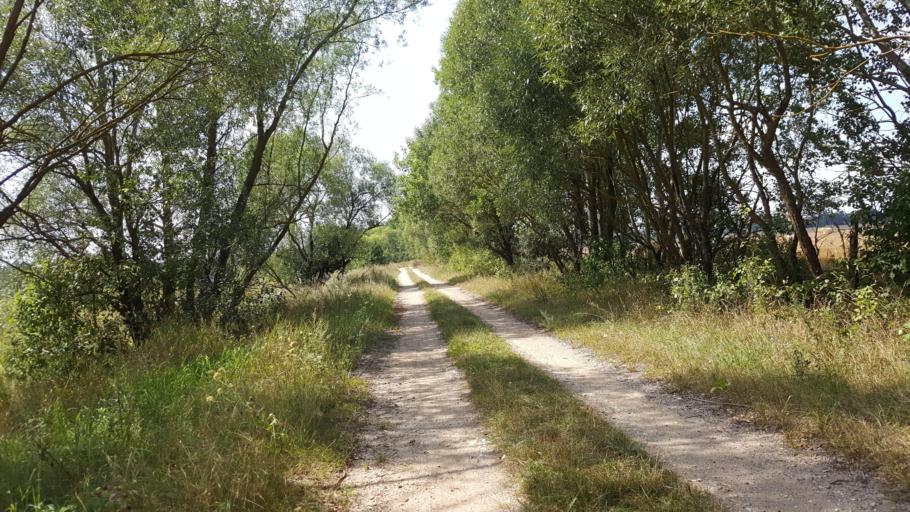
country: PL
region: Podlasie
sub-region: Powiat hajnowski
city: Hajnowka
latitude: 52.5770
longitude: 23.5696
